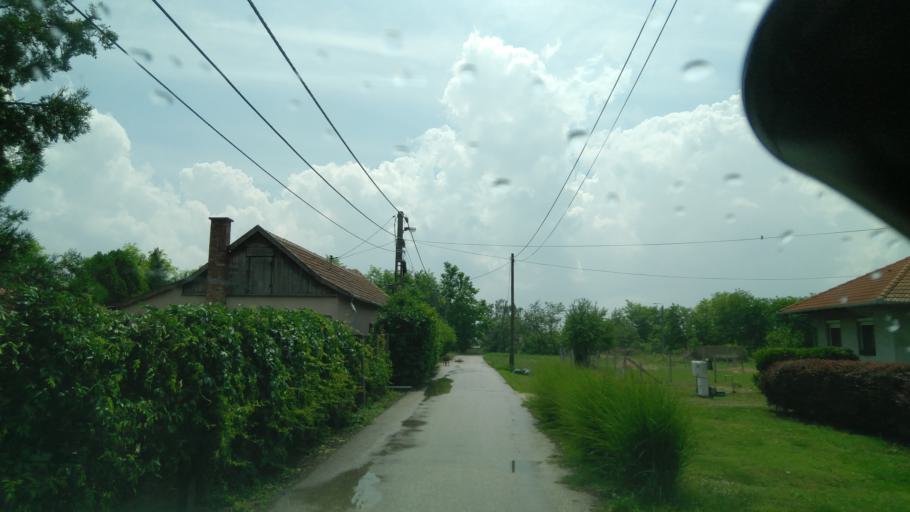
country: HU
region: Bekes
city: Bekescsaba
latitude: 46.6607
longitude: 21.1699
